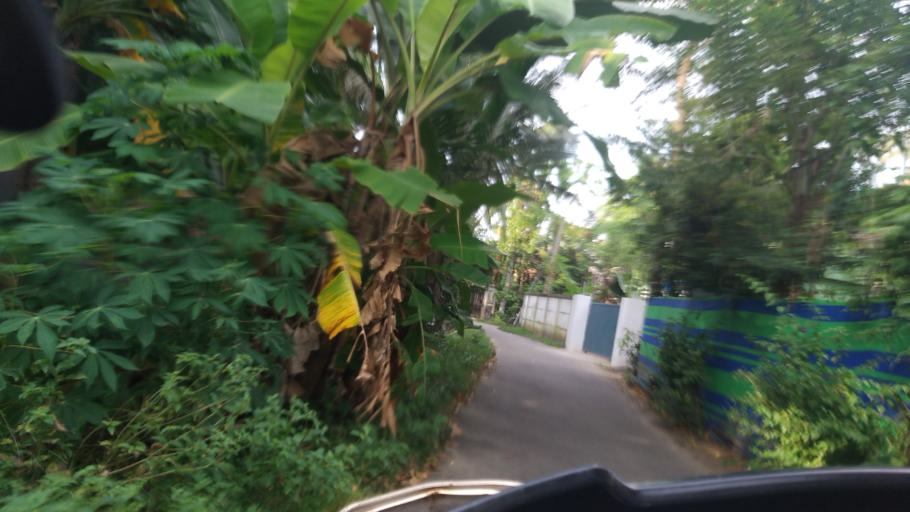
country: IN
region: Kerala
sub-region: Ernakulam
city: Elur
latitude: 10.0730
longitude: 76.2158
